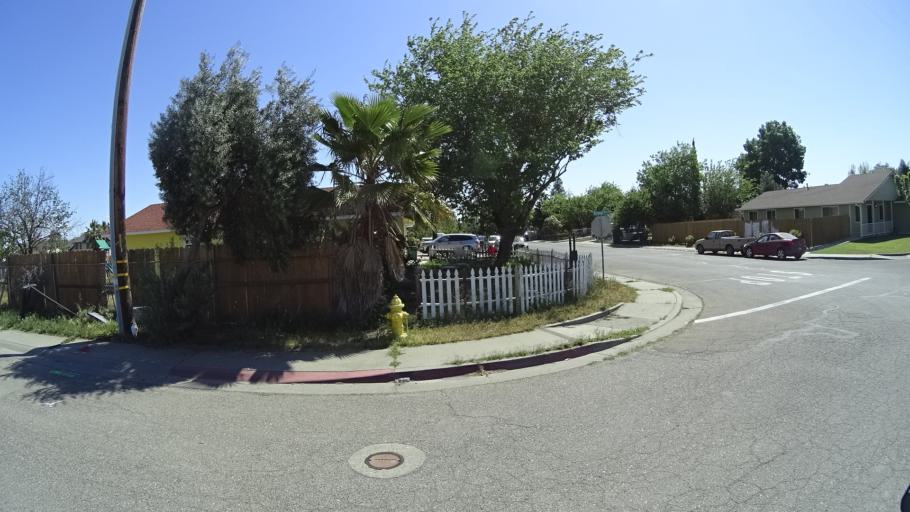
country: US
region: California
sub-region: Glenn County
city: Orland
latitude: 39.7571
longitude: -122.2015
